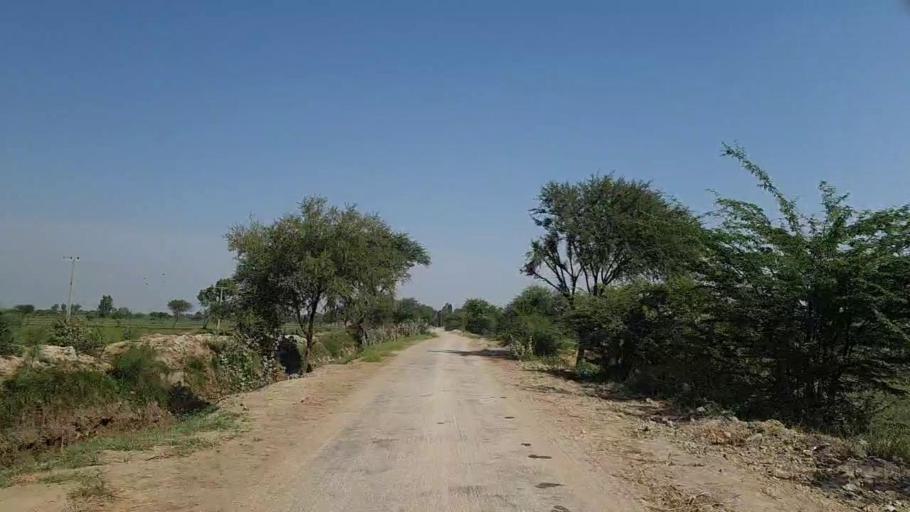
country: PK
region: Sindh
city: Mirpur Batoro
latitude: 24.6970
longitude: 68.2572
